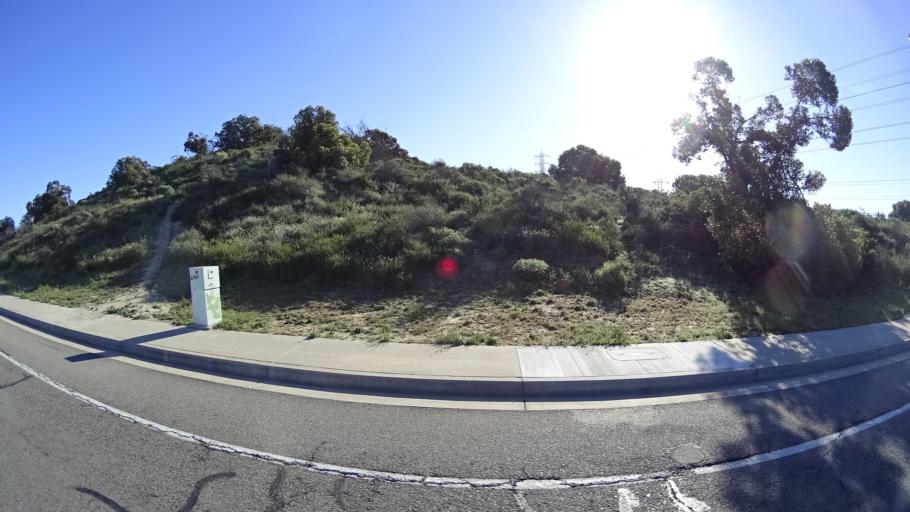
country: US
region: California
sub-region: Orange County
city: Villa Park
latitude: 33.8346
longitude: -117.7957
